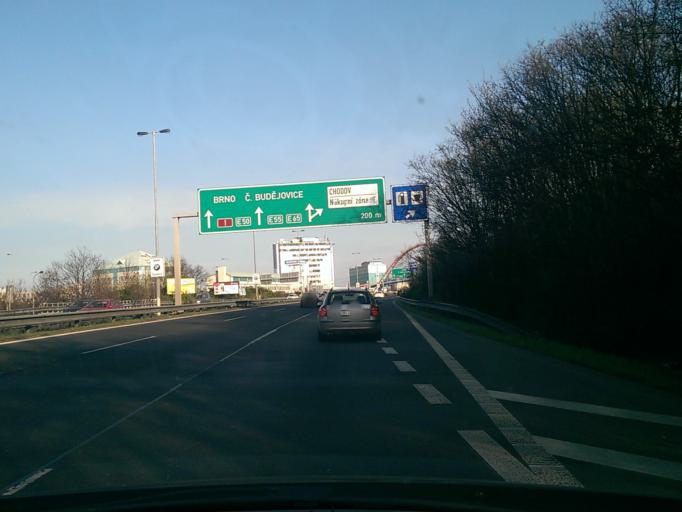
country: CZ
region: Central Bohemia
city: Vestec
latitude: 50.0393
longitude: 14.4868
